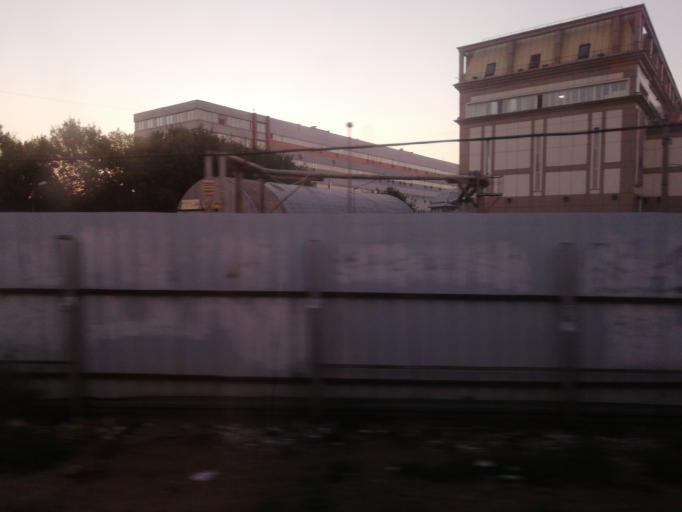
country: RU
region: Moscow
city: Mar'ina Roshcha
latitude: 55.7980
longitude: 37.5947
